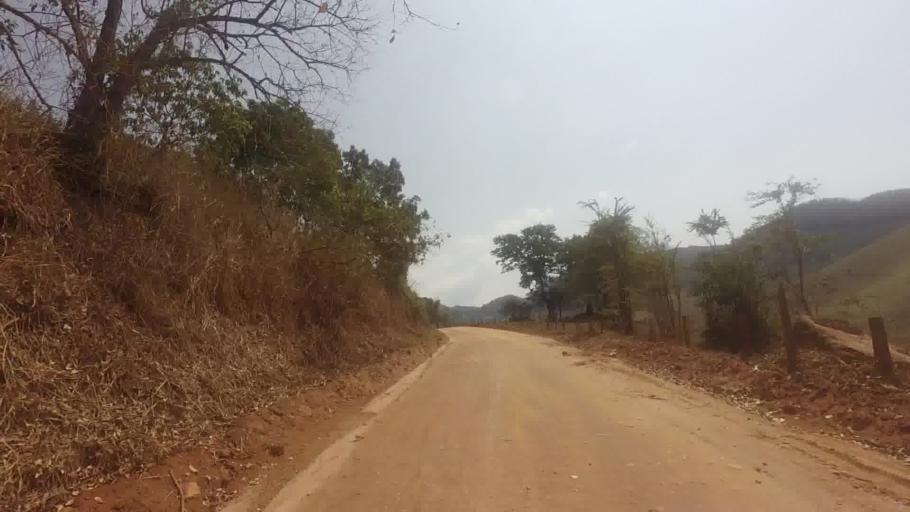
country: BR
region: Espirito Santo
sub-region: Mimoso Do Sul
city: Mimoso do Sul
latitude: -20.9469
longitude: -41.3801
